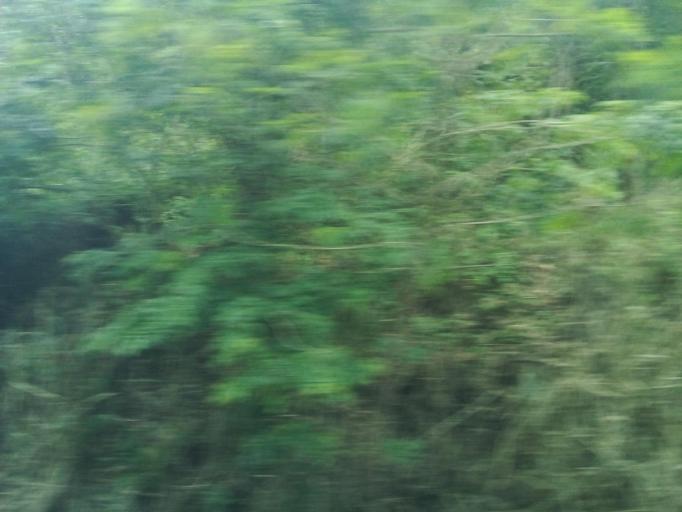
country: BR
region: Minas Gerais
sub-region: Ipaba
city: Ipaba
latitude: -19.4617
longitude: -42.4663
